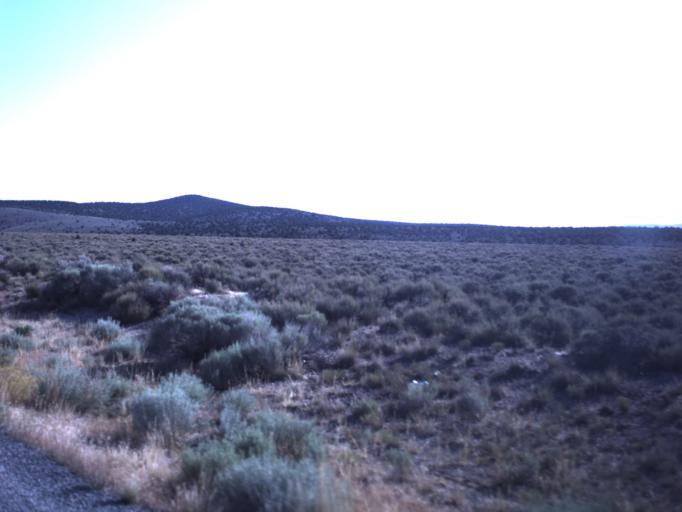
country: US
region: Utah
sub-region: Iron County
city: Parowan
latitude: 38.0140
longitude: -112.9979
